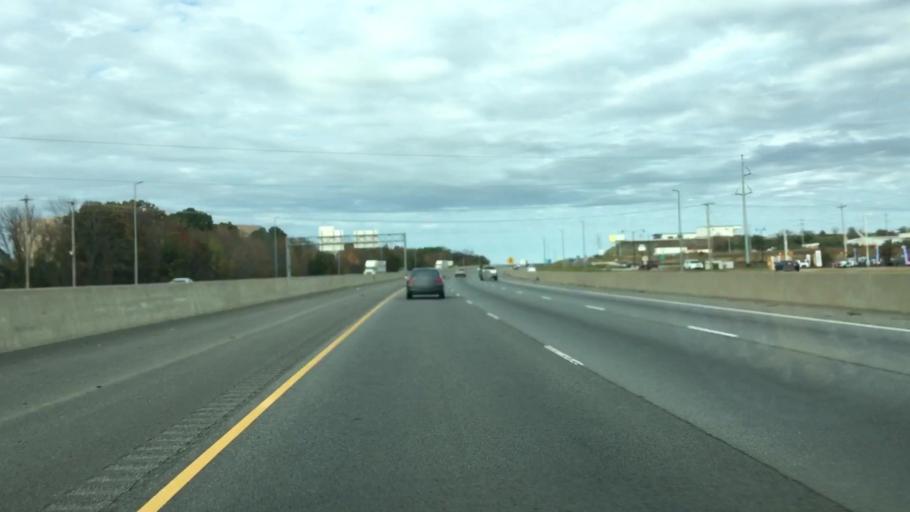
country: US
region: Arkansas
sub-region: Faulkner County
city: Conway
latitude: 35.0695
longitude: -92.4173
